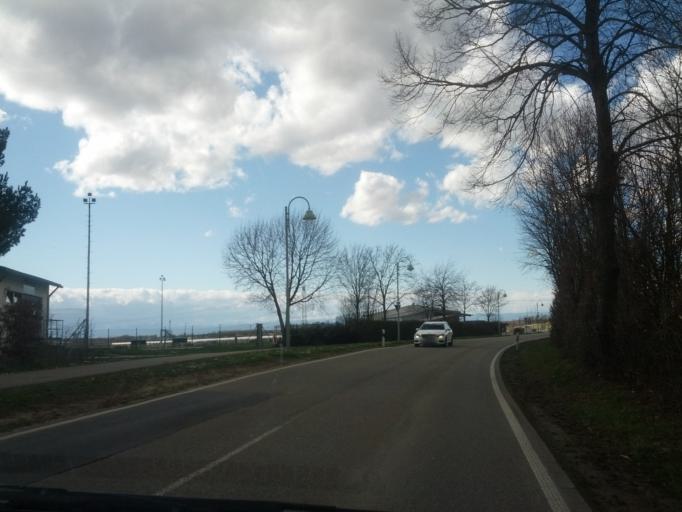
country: DE
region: Baden-Wuerttemberg
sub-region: Freiburg Region
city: Eschbach
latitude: 47.8922
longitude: 7.6509
